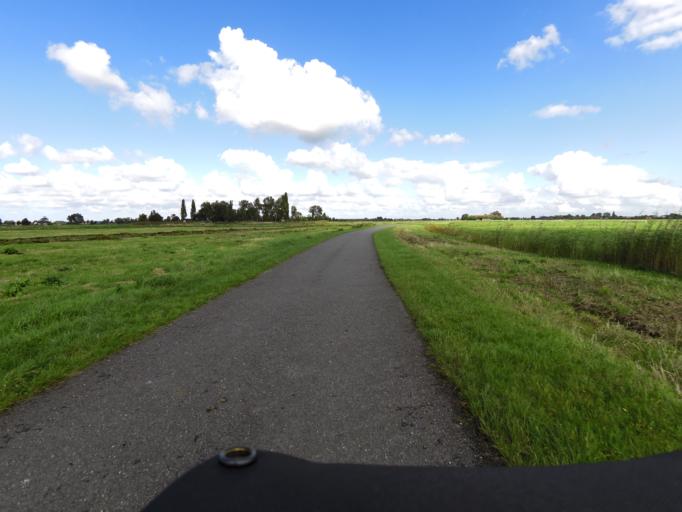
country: NL
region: South Holland
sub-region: Gemeente Vlaardingen
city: Vlaardingen
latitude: 51.9481
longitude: 4.3442
